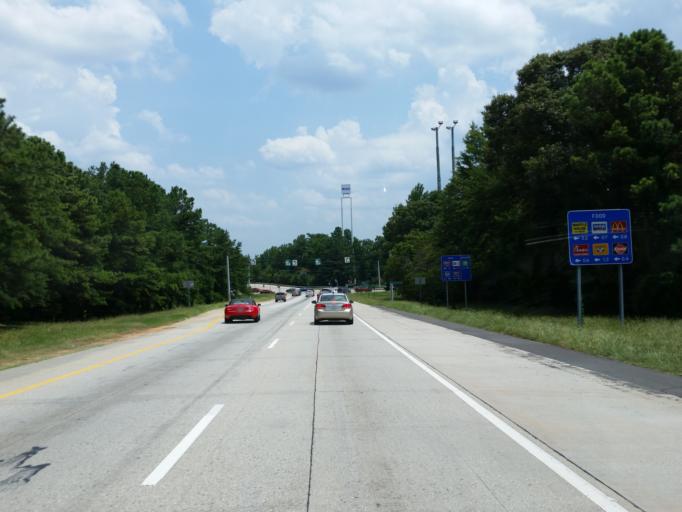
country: US
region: Georgia
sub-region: Henry County
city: Stockbridge
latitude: 33.5473
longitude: -84.2815
